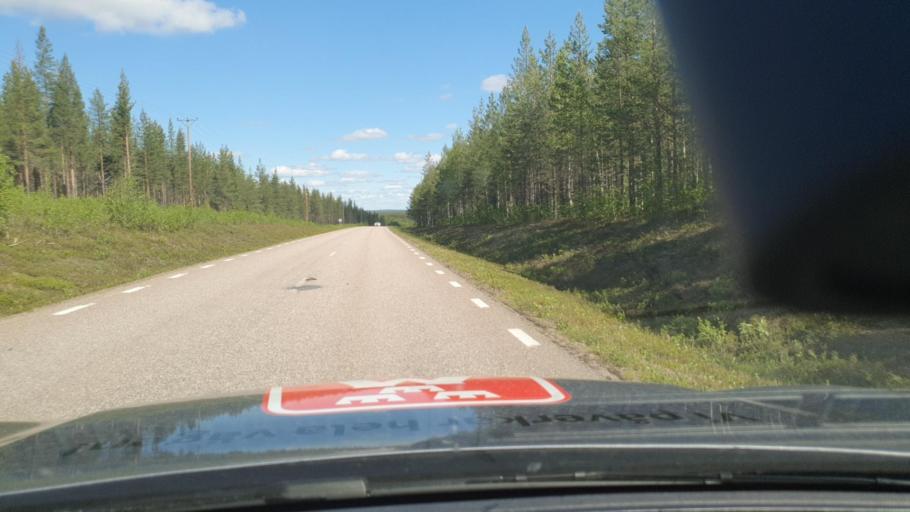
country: SE
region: Norrbotten
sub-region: Overkalix Kommun
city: OEverkalix
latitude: 67.0459
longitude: 22.5024
